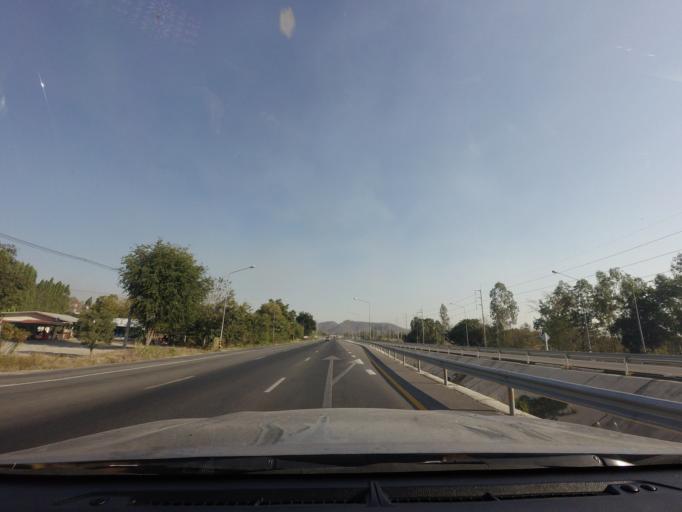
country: TH
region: Nakhon Sawan
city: Krok Phra
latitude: 15.6216
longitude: 100.1150
